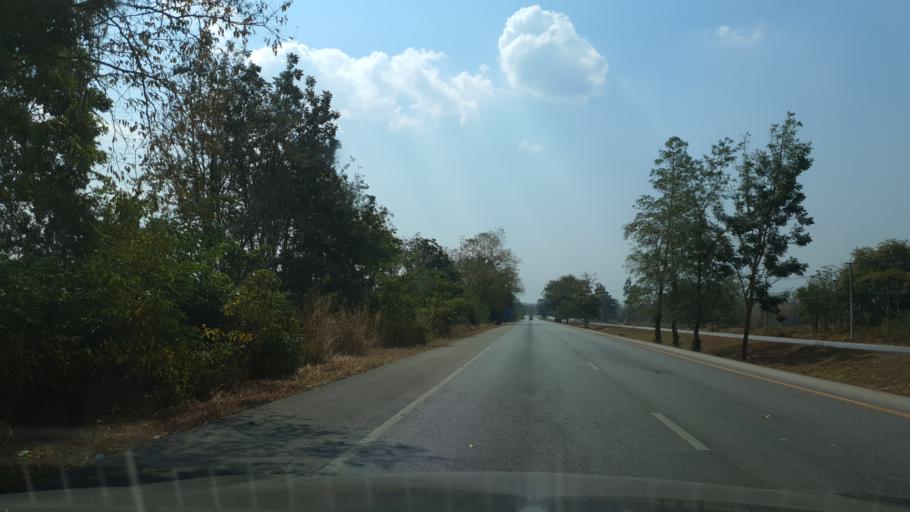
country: TH
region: Lampang
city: Mae Phrik
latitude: 17.4155
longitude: 99.1551
